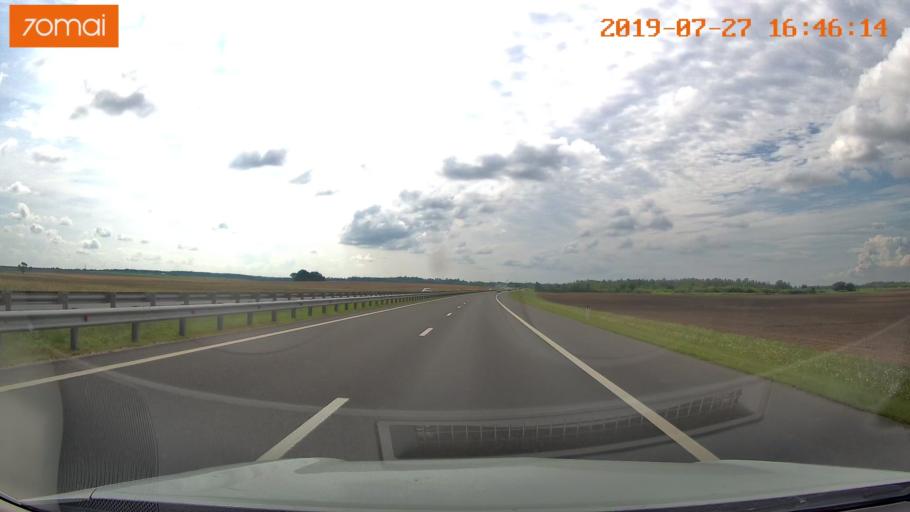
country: RU
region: Kaliningrad
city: Gvardeysk
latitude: 54.6672
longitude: 21.0274
